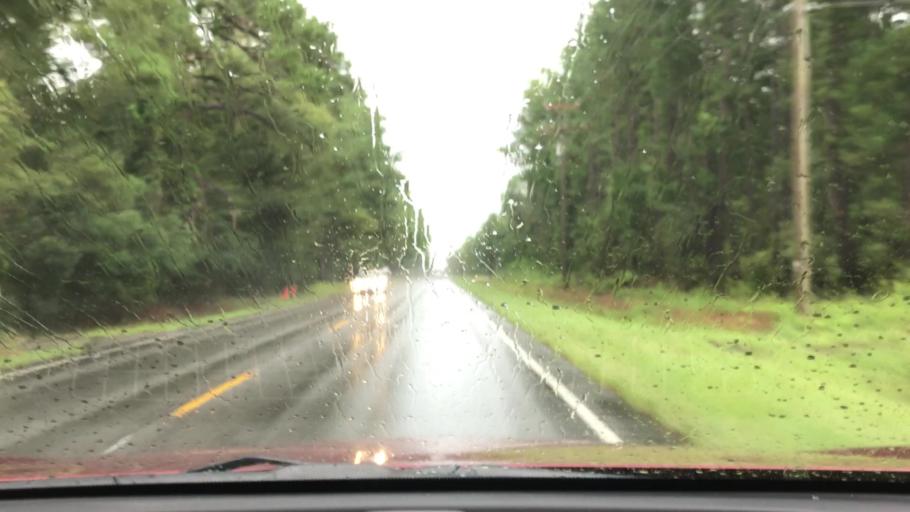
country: US
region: South Carolina
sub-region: Horry County
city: Socastee
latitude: 33.7061
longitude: -79.1029
